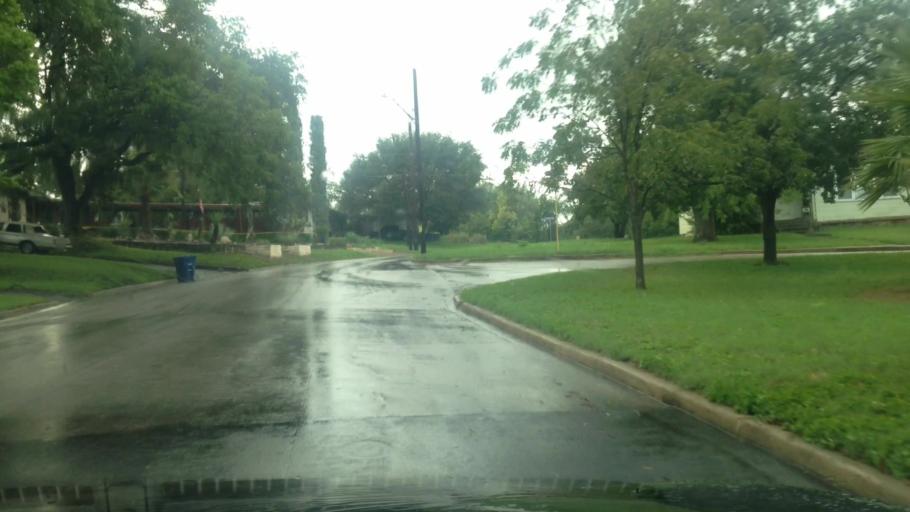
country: US
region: Texas
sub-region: Bexar County
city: Balcones Heights
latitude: 29.4804
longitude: -98.5445
